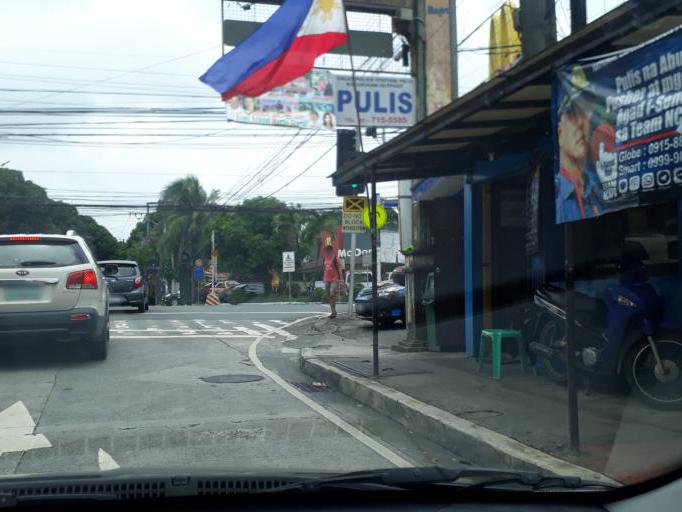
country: PH
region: Calabarzon
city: Del Monte
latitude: 14.6227
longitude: 121.0263
